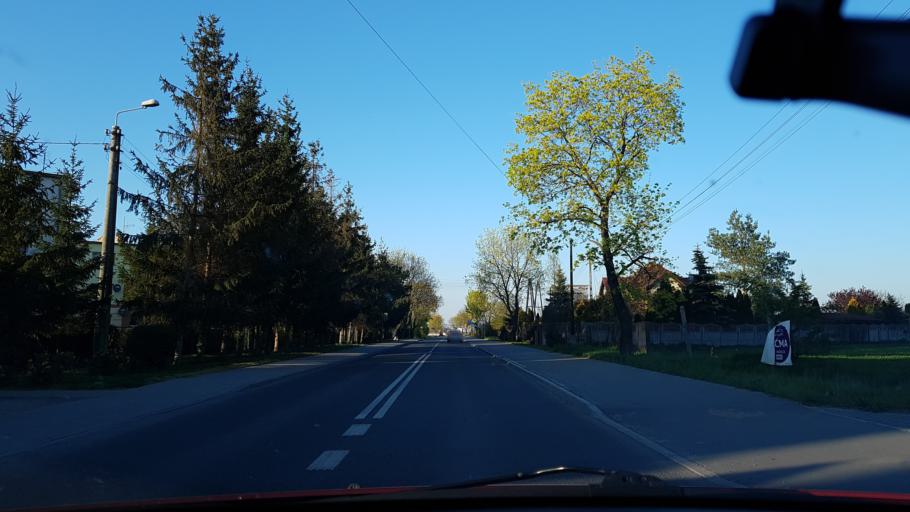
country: PL
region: Opole Voivodeship
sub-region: Powiat nyski
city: Nysa
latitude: 50.4373
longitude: 17.3082
